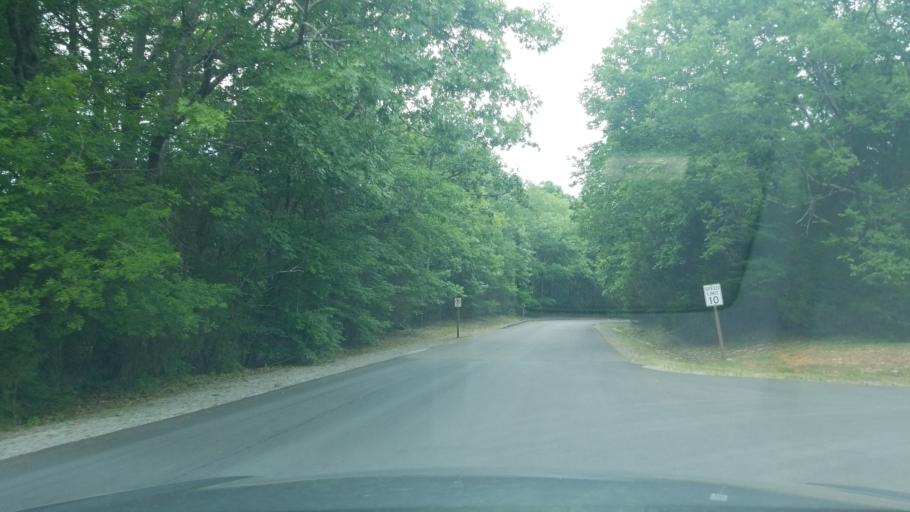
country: US
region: Tennessee
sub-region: Rutherford County
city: La Vergne
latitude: 36.0891
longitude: -86.6013
